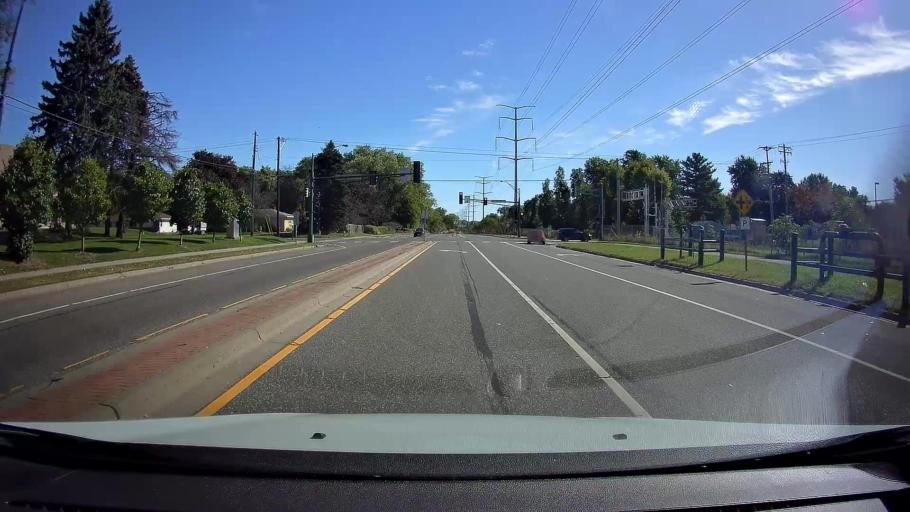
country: US
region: Minnesota
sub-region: Ramsey County
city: Roseville
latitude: 45.0207
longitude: -93.1577
